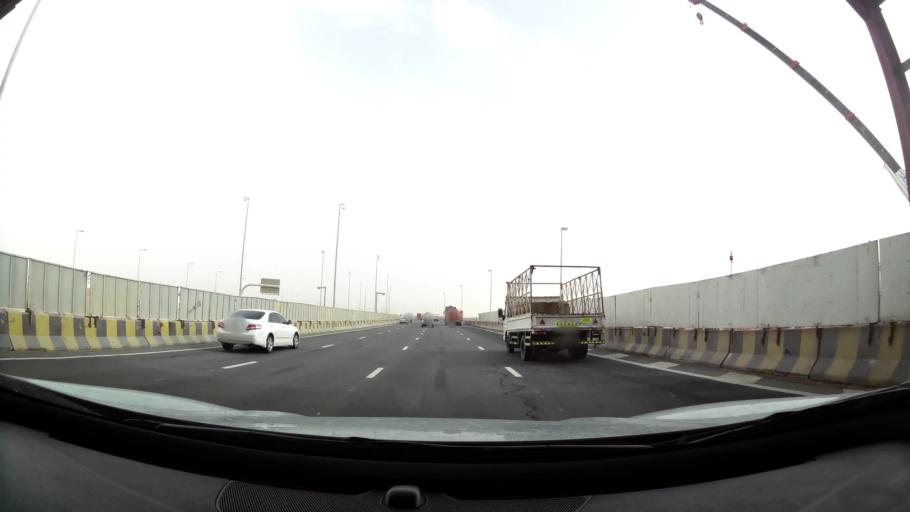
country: AE
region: Abu Dhabi
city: Abu Dhabi
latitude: 24.4570
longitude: 54.6261
